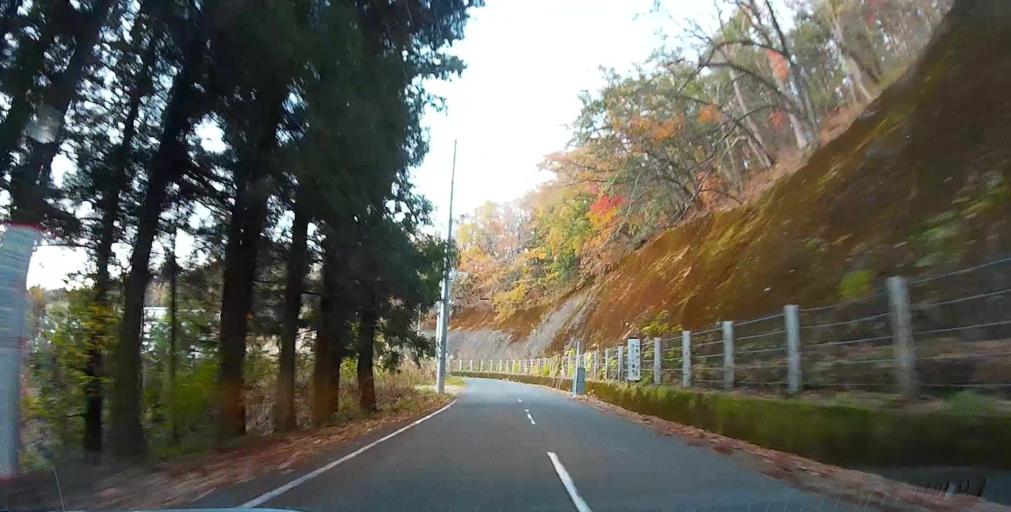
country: JP
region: Yamanashi
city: Uenohara
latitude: 35.5756
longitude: 139.1860
